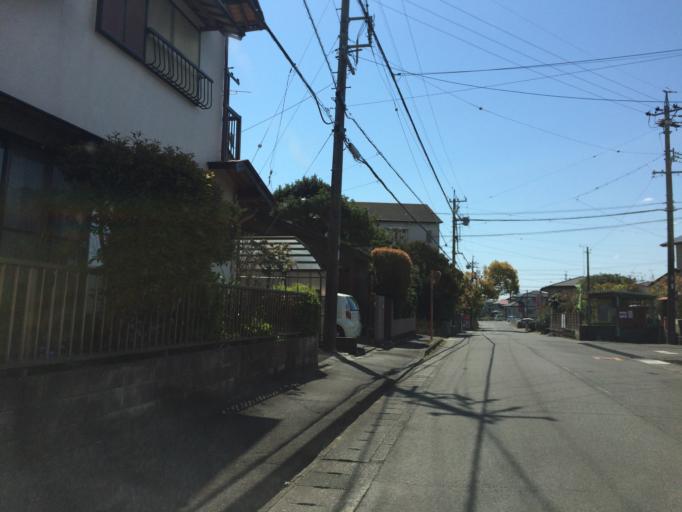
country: JP
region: Shizuoka
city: Fujieda
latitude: 34.8467
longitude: 138.2284
